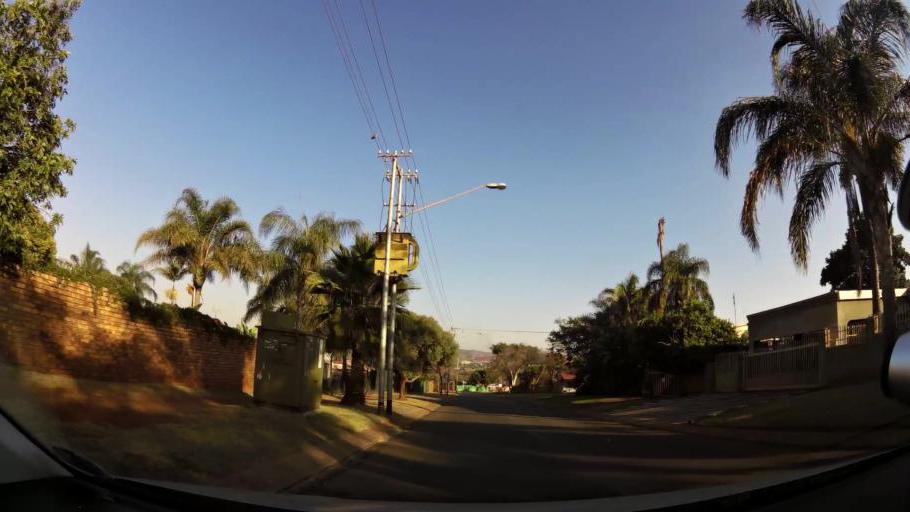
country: ZA
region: Gauteng
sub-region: City of Tshwane Metropolitan Municipality
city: Pretoria
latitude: -25.7354
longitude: 28.1277
